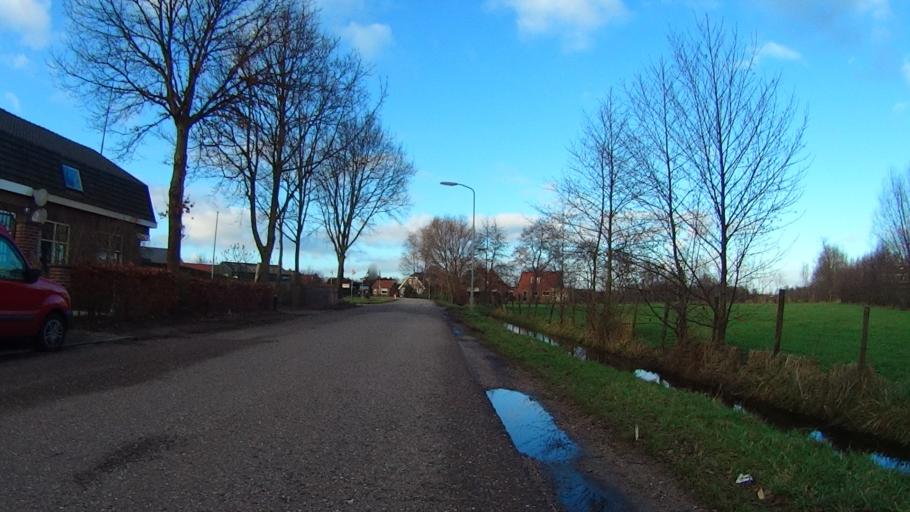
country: NL
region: Gelderland
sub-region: Gemeente Nijkerk
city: Nijkerk
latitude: 52.1914
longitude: 5.4739
